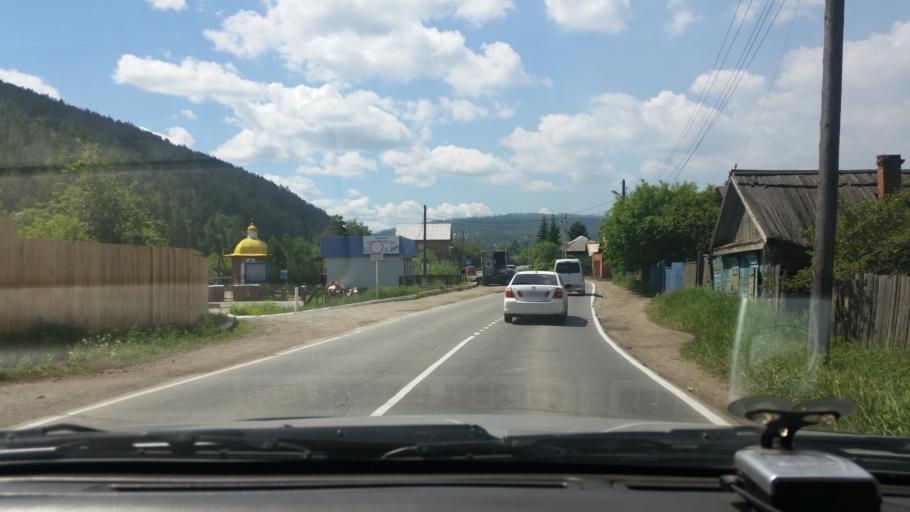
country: RU
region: Irkutsk
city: Shelekhov
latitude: 52.1574
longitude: 104.0842
